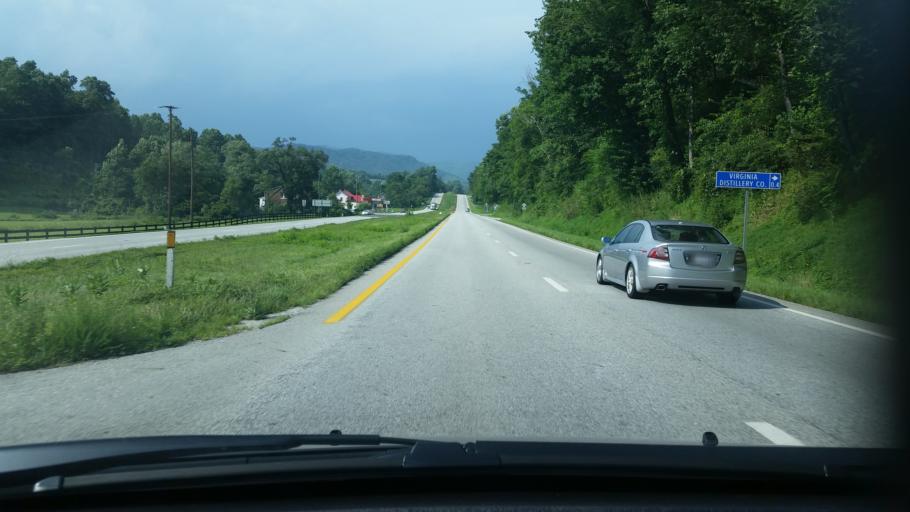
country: US
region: Virginia
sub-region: Nelson County
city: Lovingston
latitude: 37.7787
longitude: -78.8686
